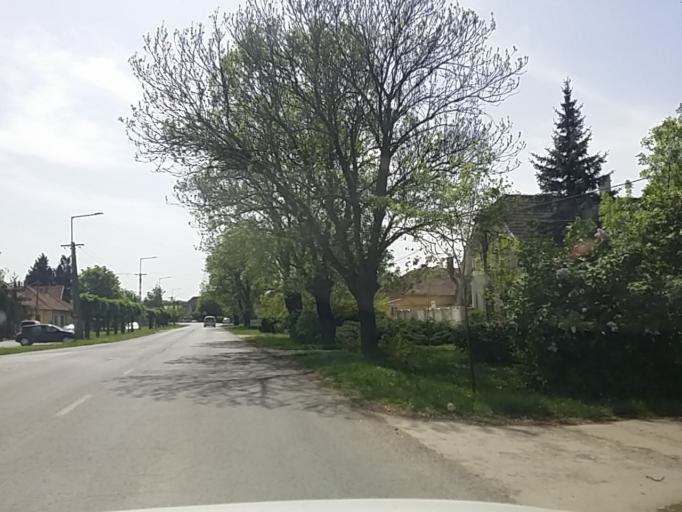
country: HU
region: Bekes
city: Gyula
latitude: 46.6511
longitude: 21.2835
